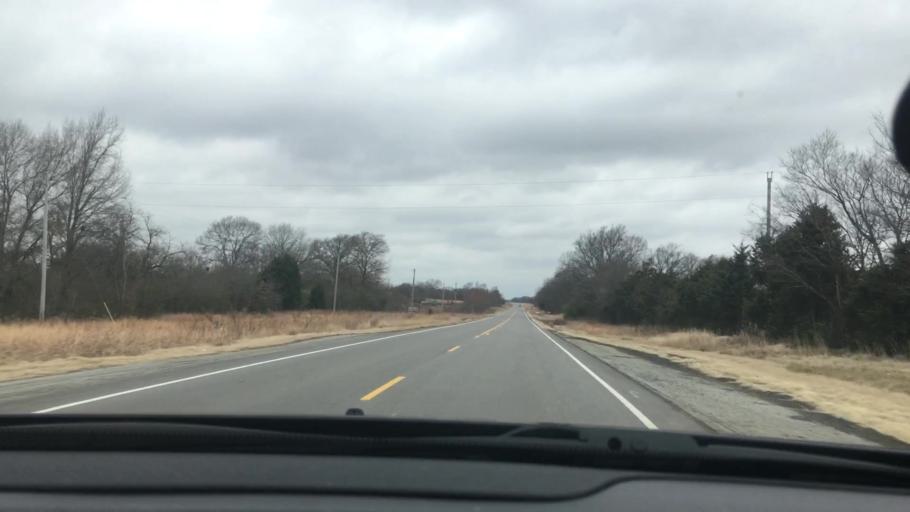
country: US
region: Oklahoma
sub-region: Atoka County
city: Atoka
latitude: 34.3749
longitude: -96.1610
